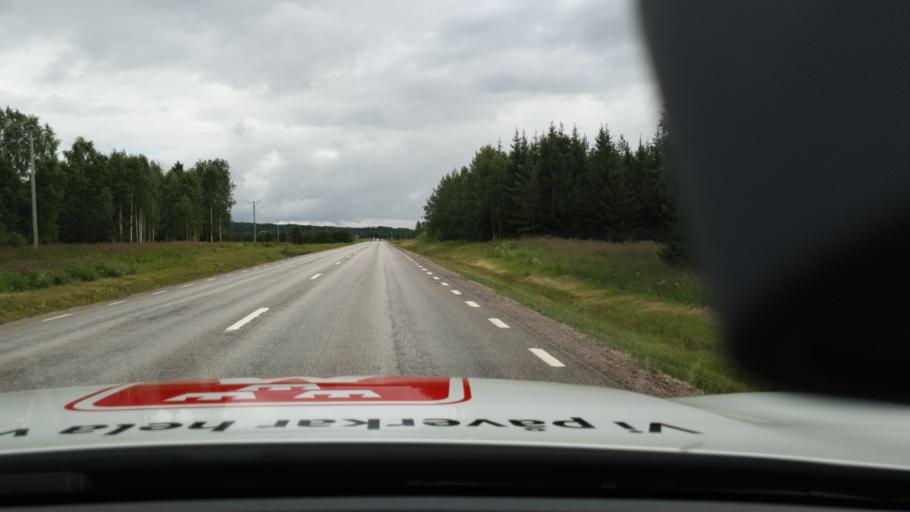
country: SE
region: Norrbotten
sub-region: Pitea Kommun
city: Rosvik
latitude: 65.5746
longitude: 21.7363
